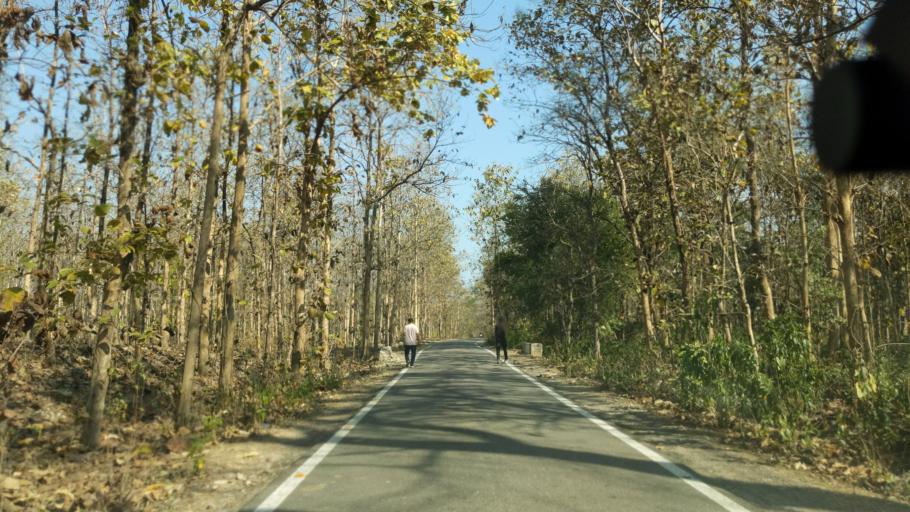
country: IN
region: Uttarakhand
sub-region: Naini Tal
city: Ramnagar
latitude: 29.4268
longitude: 79.1398
